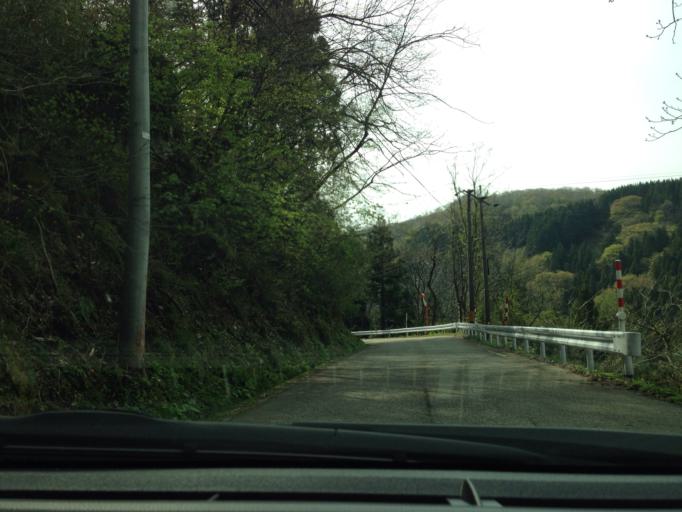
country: JP
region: Toyama
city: Fukumitsu
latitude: 36.4831
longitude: 136.8197
